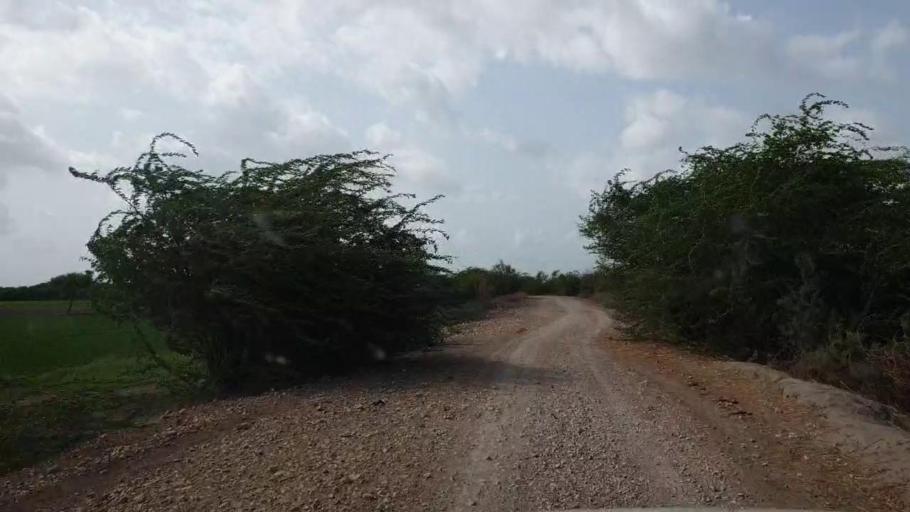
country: PK
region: Sindh
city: Kario
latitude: 24.6961
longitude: 68.6485
